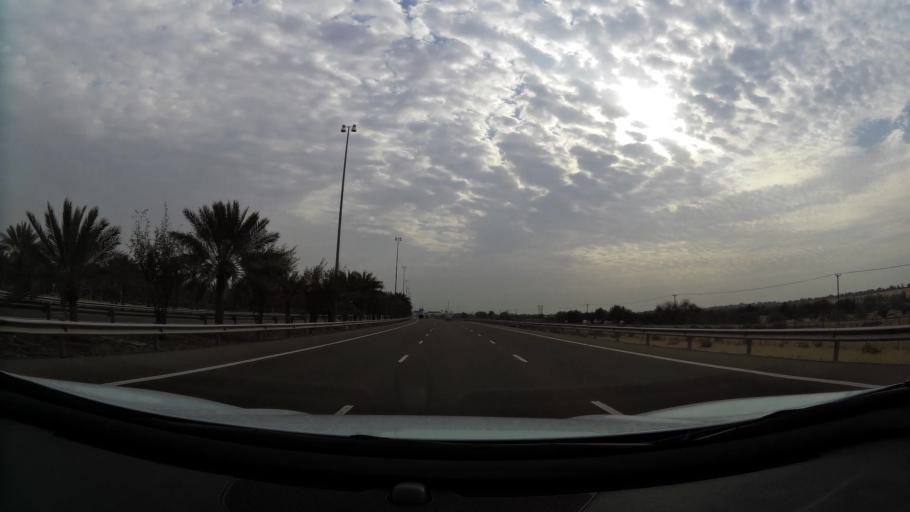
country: AE
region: Abu Dhabi
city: Al Ain
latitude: 24.1684
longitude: 55.0892
